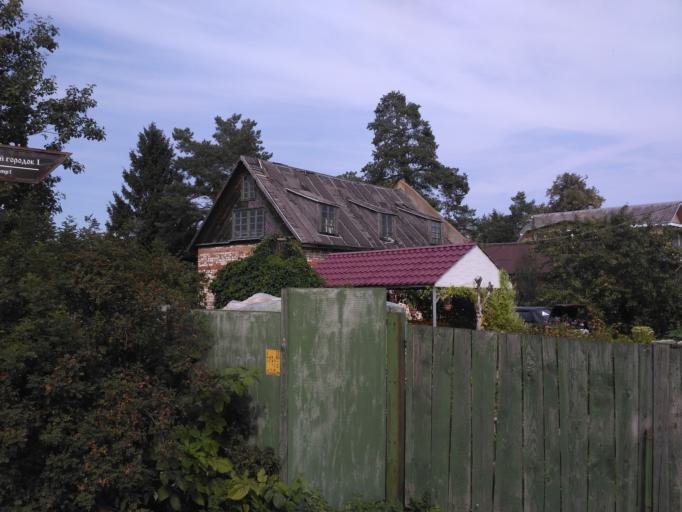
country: RU
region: Moskovskaya
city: Sergiyev Posad
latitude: 56.3142
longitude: 38.1257
